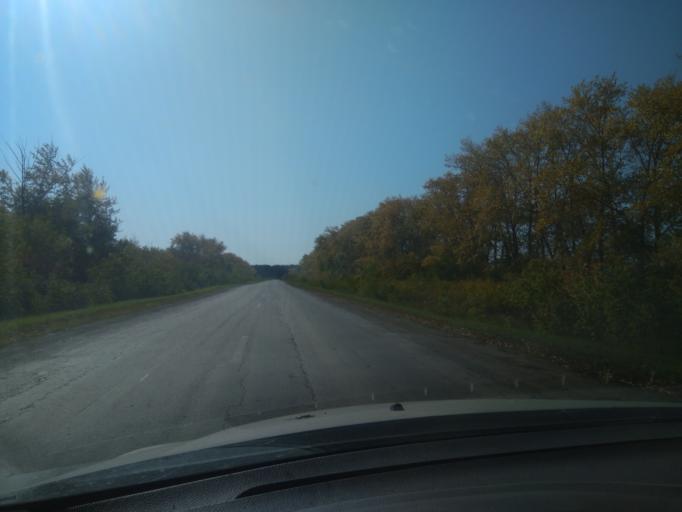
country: RU
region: Sverdlovsk
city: Pokrovskoye
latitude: 56.4593
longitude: 61.6095
